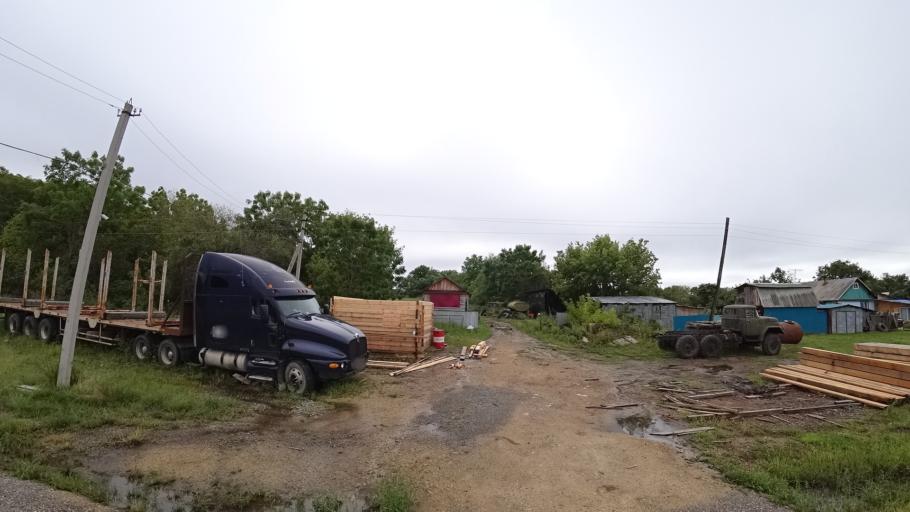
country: RU
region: Primorskiy
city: Monastyrishche
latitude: 44.0819
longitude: 132.5909
